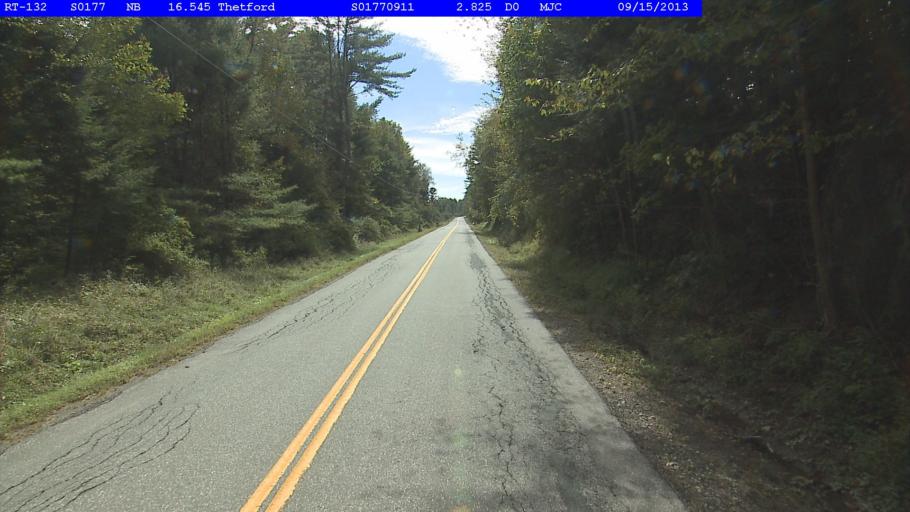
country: US
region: New Hampshire
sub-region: Grafton County
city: Hanover
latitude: 43.8170
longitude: -72.2777
